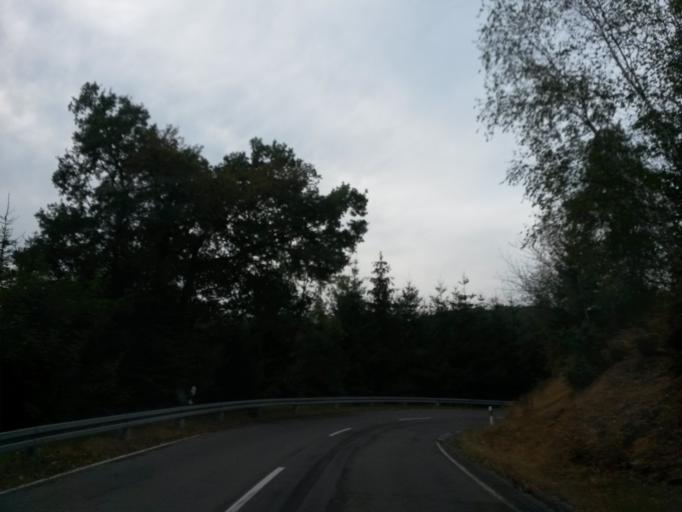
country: DE
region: North Rhine-Westphalia
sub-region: Regierungsbezirk Koln
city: Gummersbach
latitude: 51.0001
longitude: 7.5744
